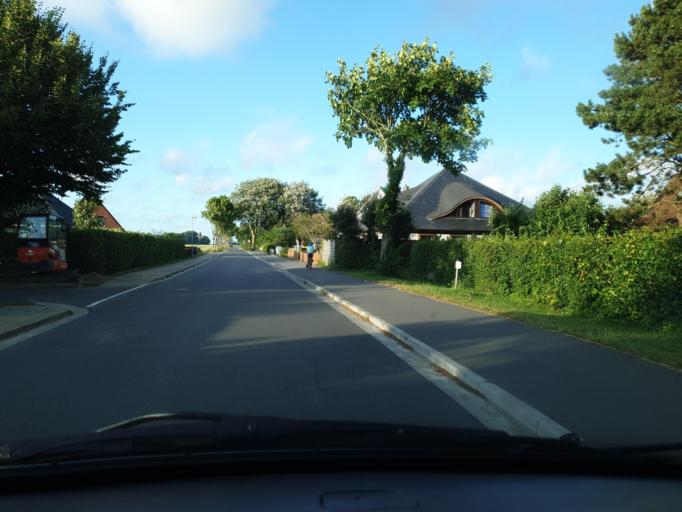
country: DE
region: Schleswig-Holstein
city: Busumer Deichhausen
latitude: 54.1383
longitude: 8.8933
